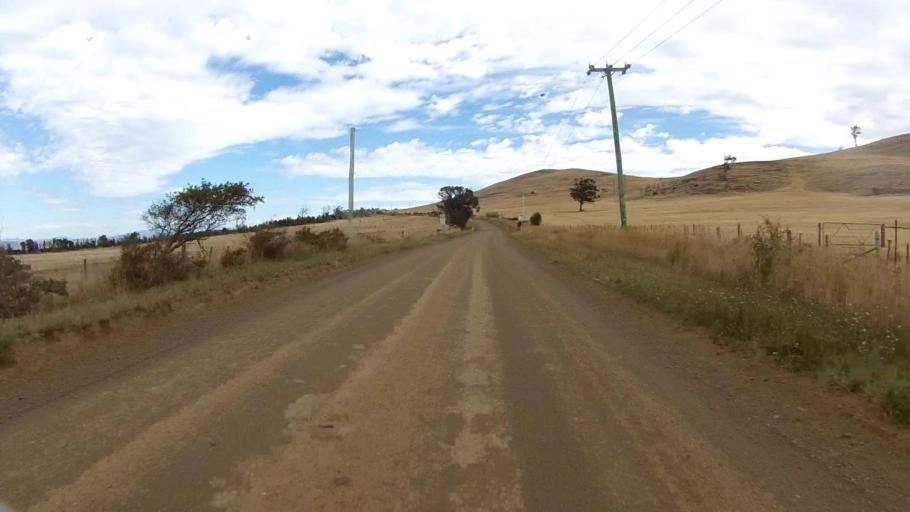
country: AU
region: Tasmania
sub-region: Sorell
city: Sorell
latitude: -42.8971
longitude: 147.7542
